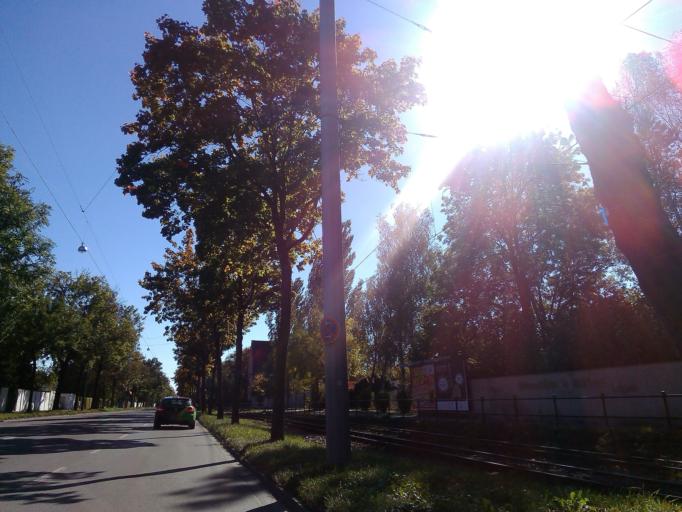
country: DE
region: Bavaria
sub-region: Swabia
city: Augsburg
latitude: 48.3338
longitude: 10.9078
